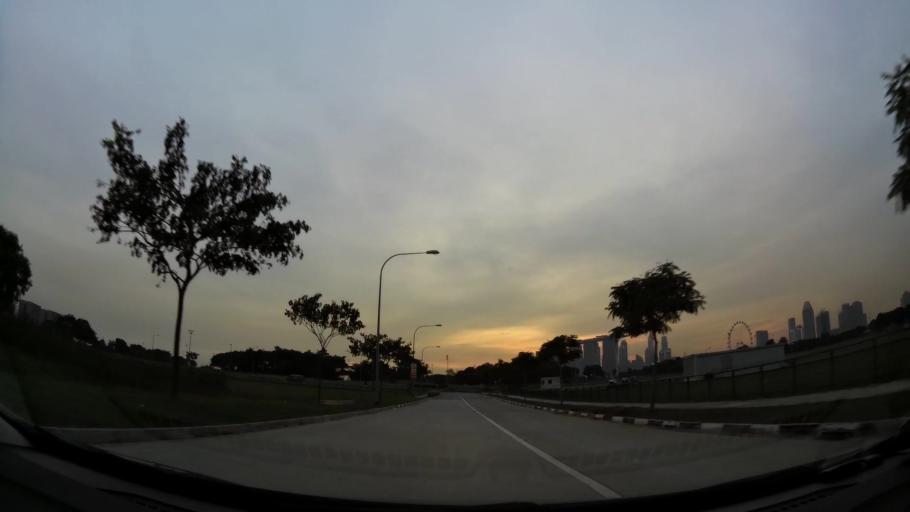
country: SG
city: Singapore
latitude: 1.2883
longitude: 103.8779
